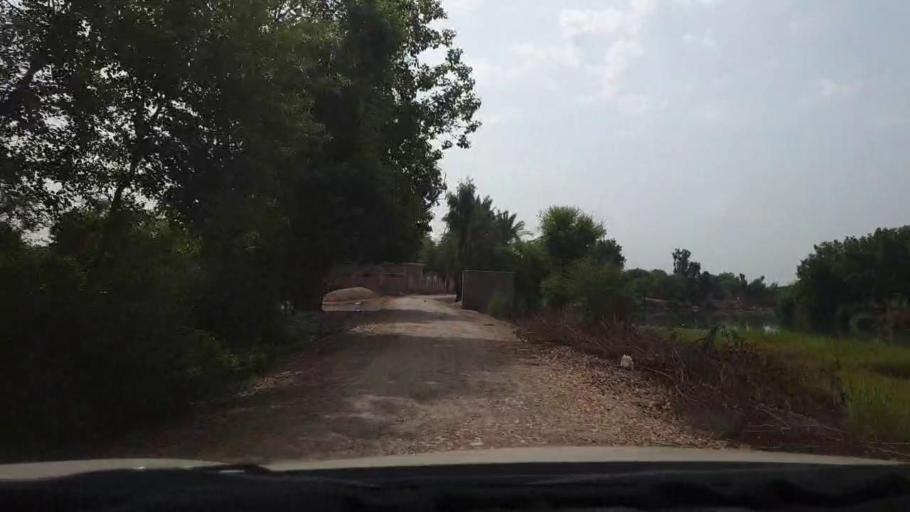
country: PK
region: Sindh
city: Dokri
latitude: 27.3897
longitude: 68.1209
